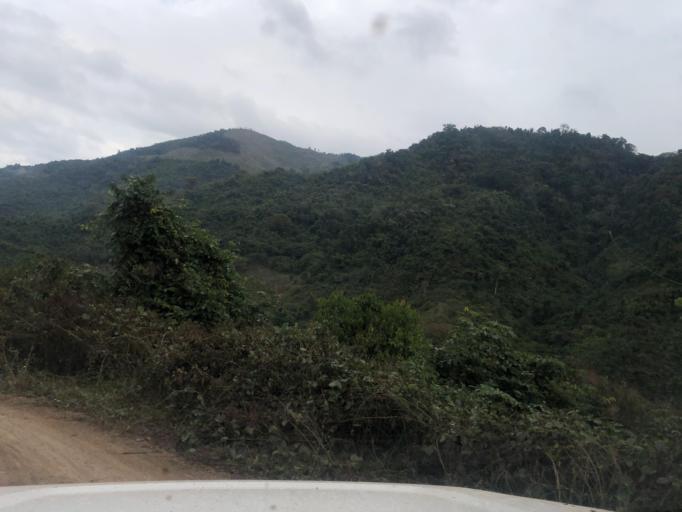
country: LA
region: Phongsali
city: Khoa
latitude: 21.2934
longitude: 102.5849
